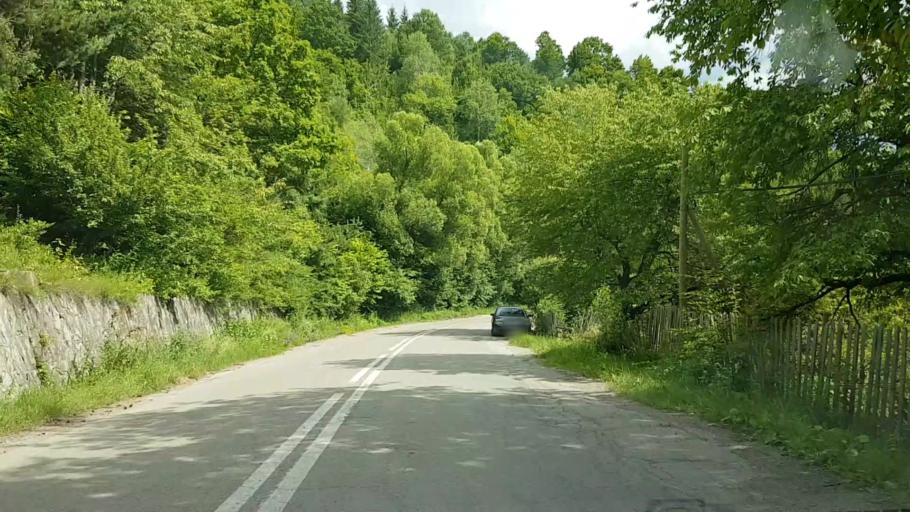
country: RO
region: Neamt
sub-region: Comuna Hangu
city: Hangu
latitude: 47.0286
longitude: 26.0675
